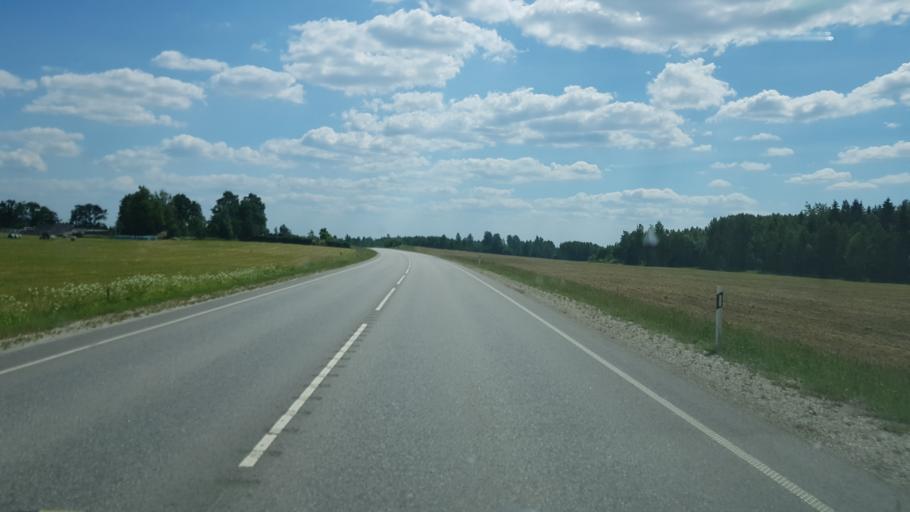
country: EE
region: Vorumaa
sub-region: Voru linn
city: Voru
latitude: 57.9268
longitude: 26.8010
